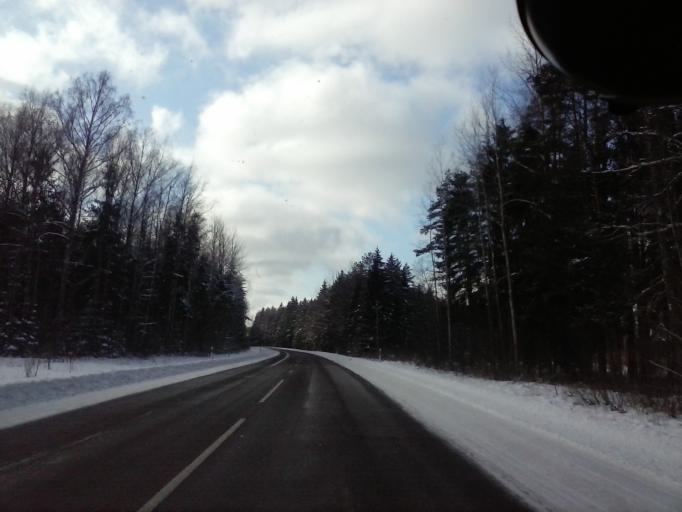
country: EE
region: Viljandimaa
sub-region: Moisakuela linn
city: Moisakula
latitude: 58.2438
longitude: 25.1347
